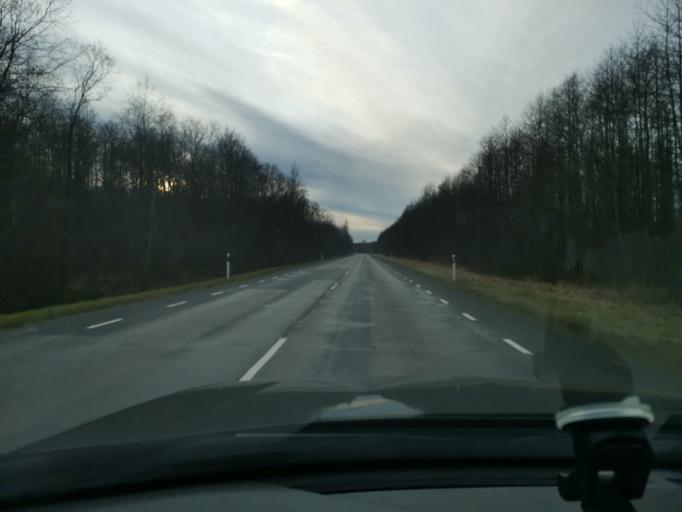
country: EE
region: Ida-Virumaa
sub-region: Narva-Joesuu linn
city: Narva-Joesuu
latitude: 59.3262
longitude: 27.9280
